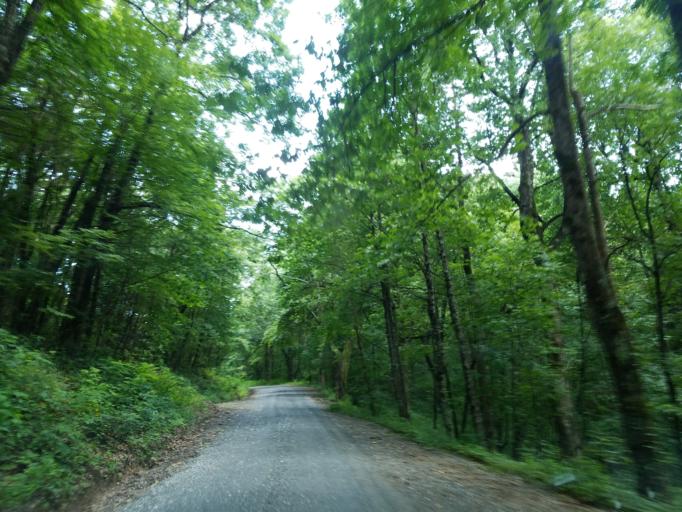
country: US
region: Georgia
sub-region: Dawson County
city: Dawsonville
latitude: 34.6386
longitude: -84.1957
